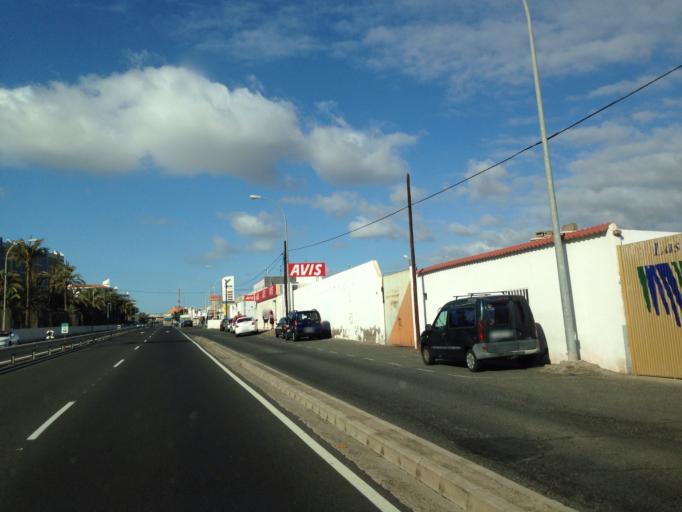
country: ES
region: Canary Islands
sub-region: Provincia de Las Palmas
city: Playa del Ingles
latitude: 27.7647
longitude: -15.5673
